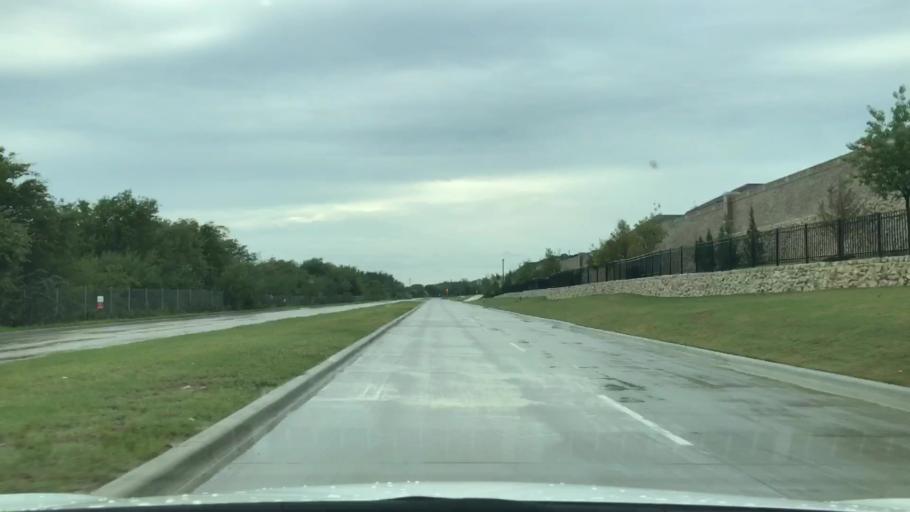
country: US
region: Texas
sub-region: Dallas County
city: Coppell
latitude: 32.9057
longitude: -97.0021
